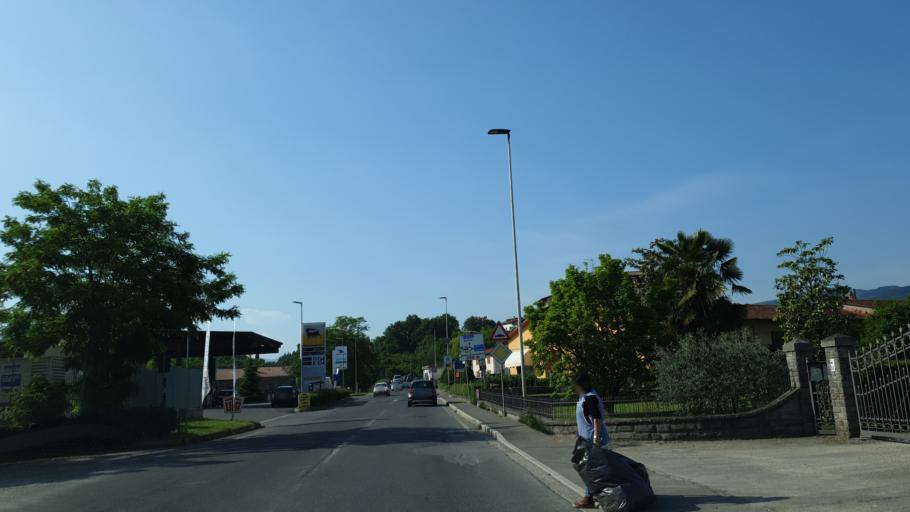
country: IT
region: Tuscany
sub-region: Province of Arezzo
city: Poppi
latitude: 43.7238
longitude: 11.7753
